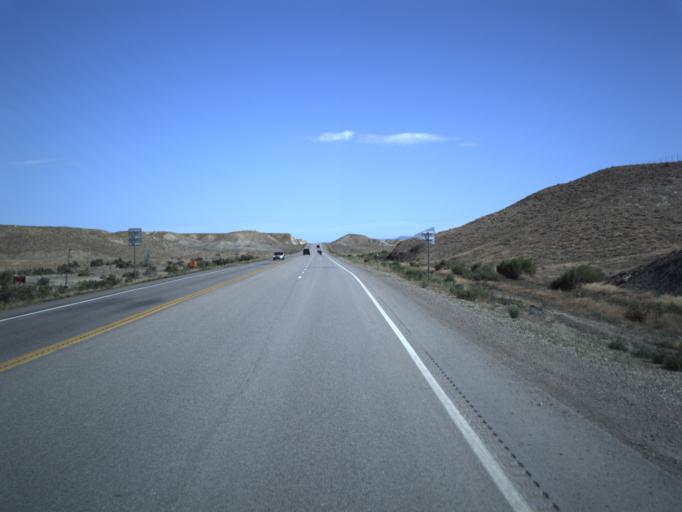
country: US
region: Utah
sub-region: Carbon County
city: East Carbon City
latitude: 39.2695
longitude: -110.3450
